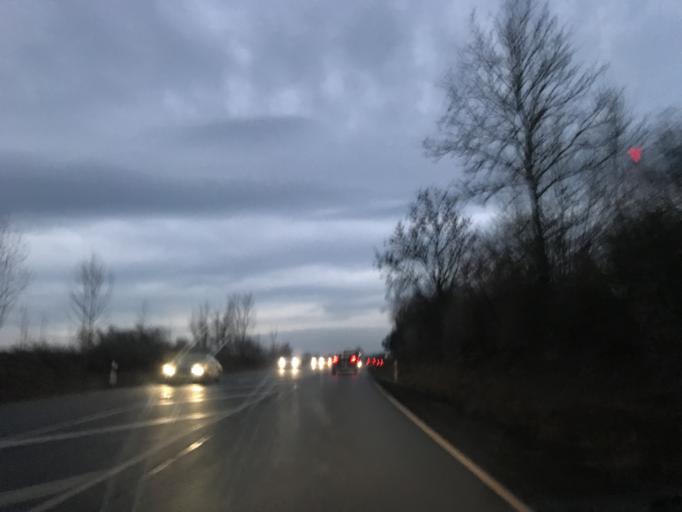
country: DE
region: Hesse
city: Grebenstein
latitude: 51.4671
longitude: 9.4038
